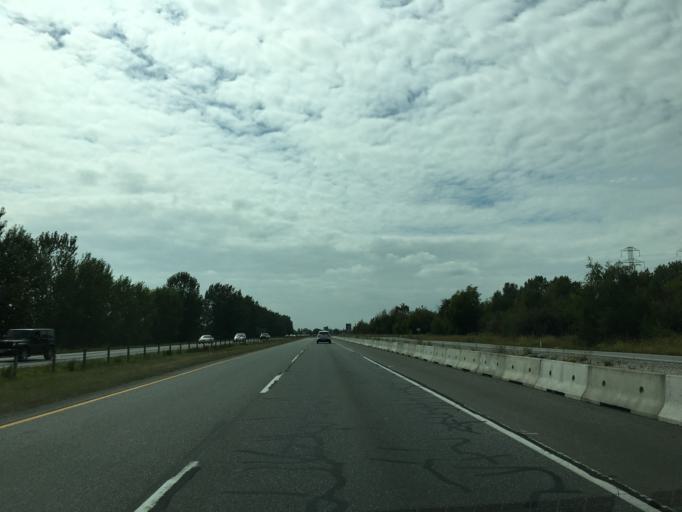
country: CA
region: British Columbia
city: Ladner
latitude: 49.0905
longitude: -122.9898
